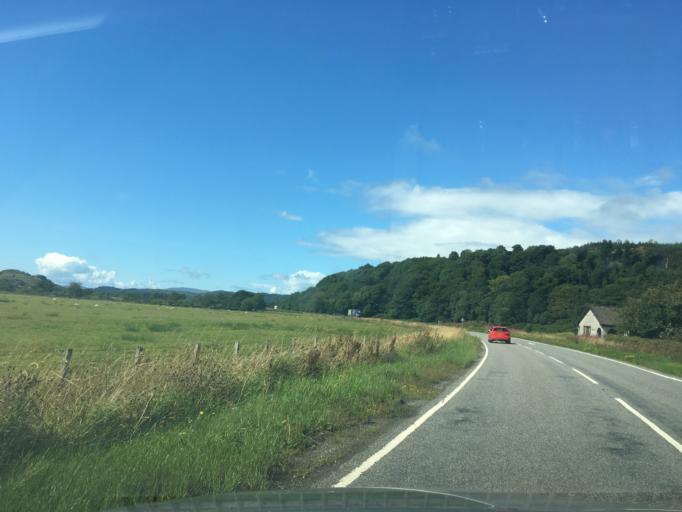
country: GB
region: Scotland
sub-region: Argyll and Bute
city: Lochgilphead
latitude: 56.0810
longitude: -5.4532
